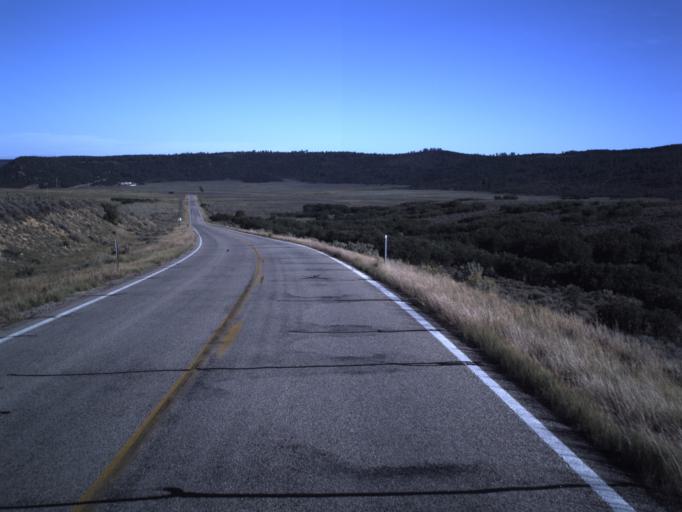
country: US
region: Utah
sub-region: Grand County
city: Moab
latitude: 38.3357
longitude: -109.1597
